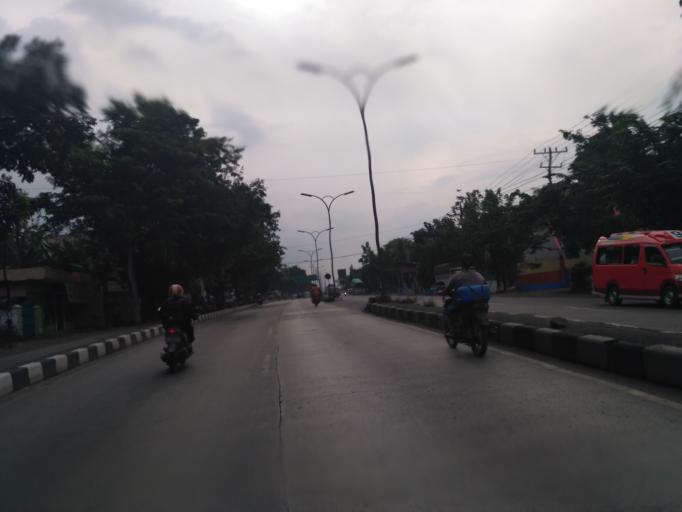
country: ID
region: Central Java
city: Semarang
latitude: -6.9720
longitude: 110.2936
